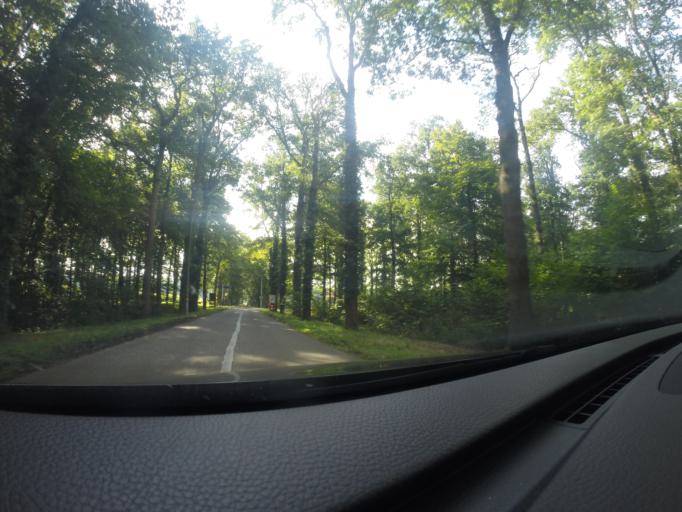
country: NL
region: Gelderland
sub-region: Gemeente Bronckhorst
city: Zelhem
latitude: 51.9644
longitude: 6.3535
